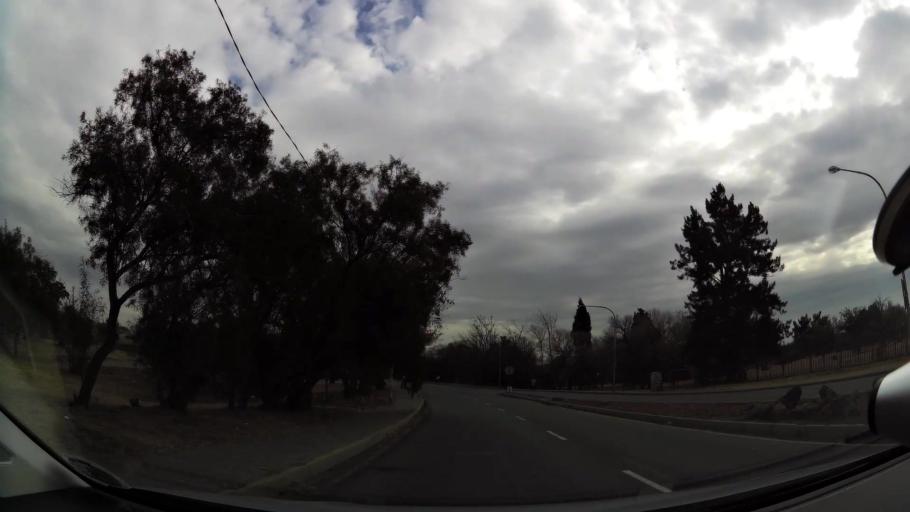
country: ZA
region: Orange Free State
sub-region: Fezile Dabi District Municipality
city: Kroonstad
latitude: -27.6726
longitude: 27.2382
